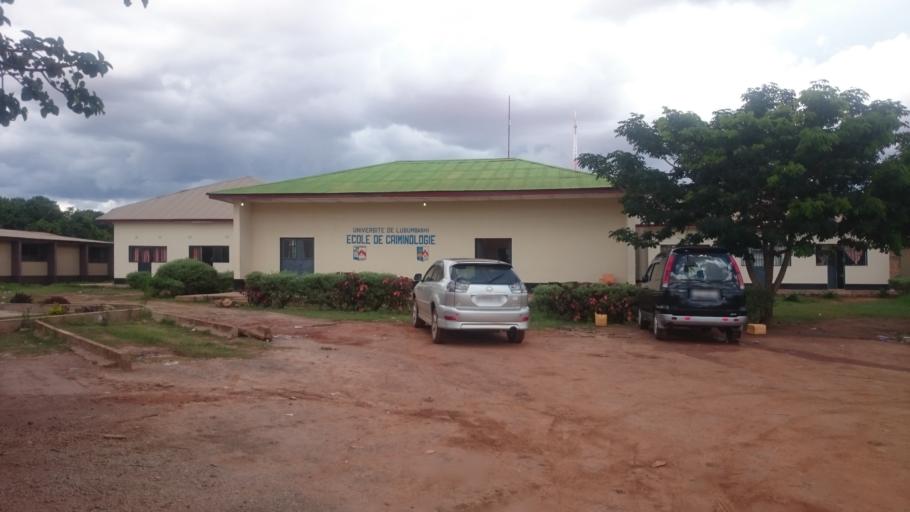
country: CD
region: Katanga
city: Lubumbashi
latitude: -11.6312
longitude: 27.4849
